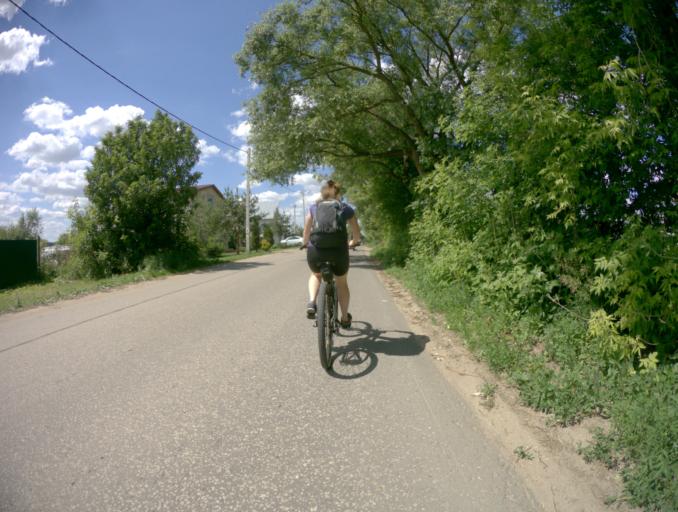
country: RU
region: Vladimir
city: Bogolyubovo
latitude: 56.1911
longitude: 40.4958
